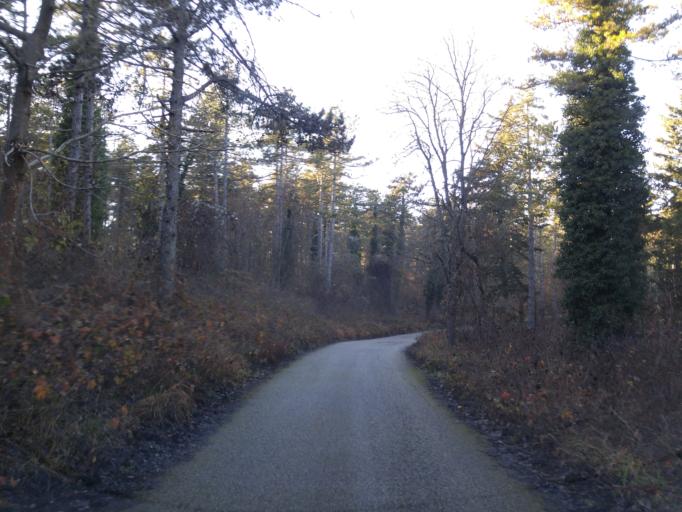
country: IT
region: The Marches
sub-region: Provincia di Pesaro e Urbino
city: Isola del Piano
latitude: 43.7047
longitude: 12.7596
